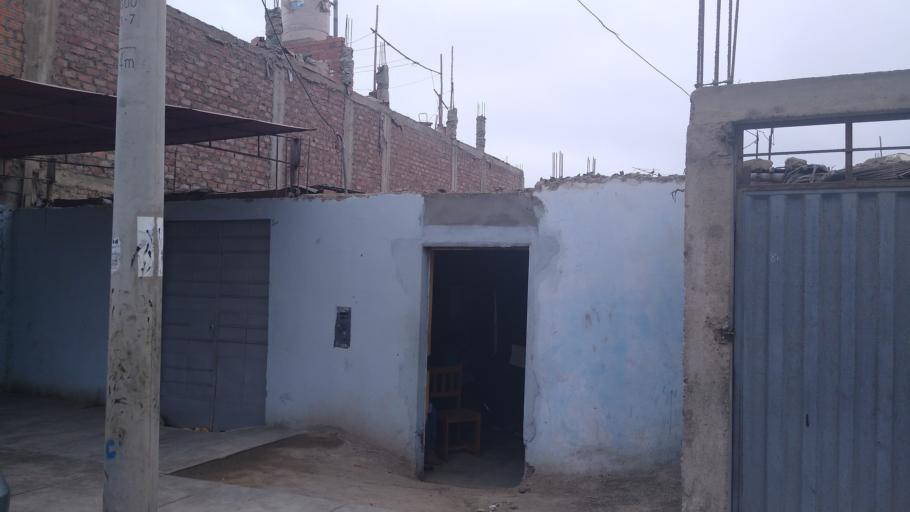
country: PE
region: Lima
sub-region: Provincia de Canete
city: San Vicente de Canete
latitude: -13.0757
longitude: -76.3909
